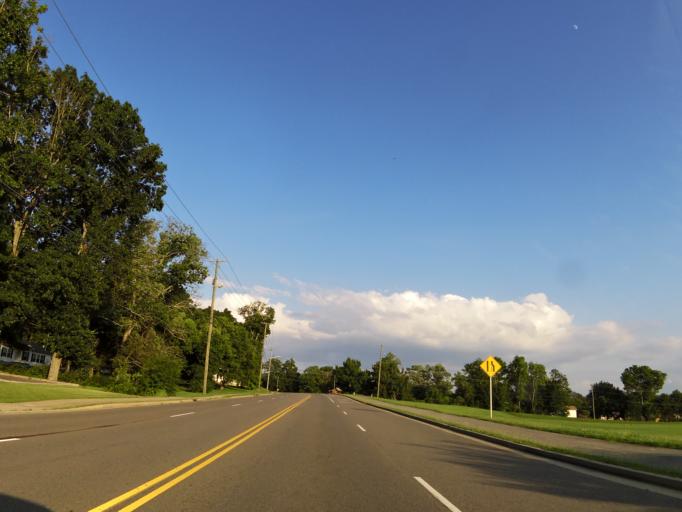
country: US
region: Tennessee
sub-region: Knox County
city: Knoxville
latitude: 35.9892
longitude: -83.9986
